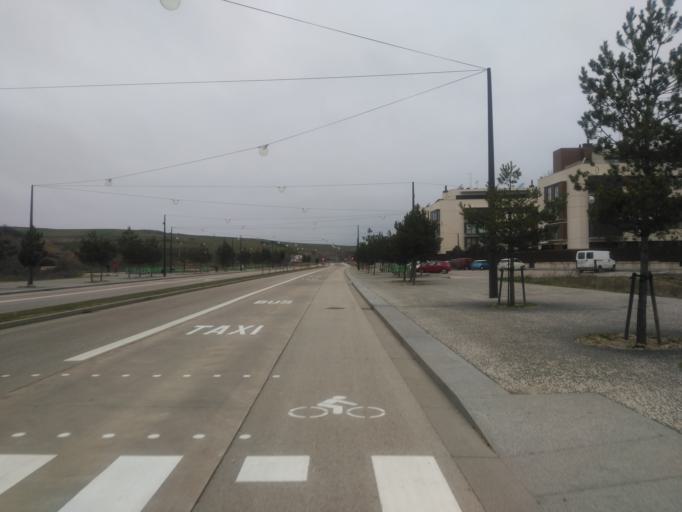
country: ES
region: Castille and Leon
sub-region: Provincia de Burgos
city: Villagonzalo-Pedernales
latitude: 42.3331
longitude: -3.7139
